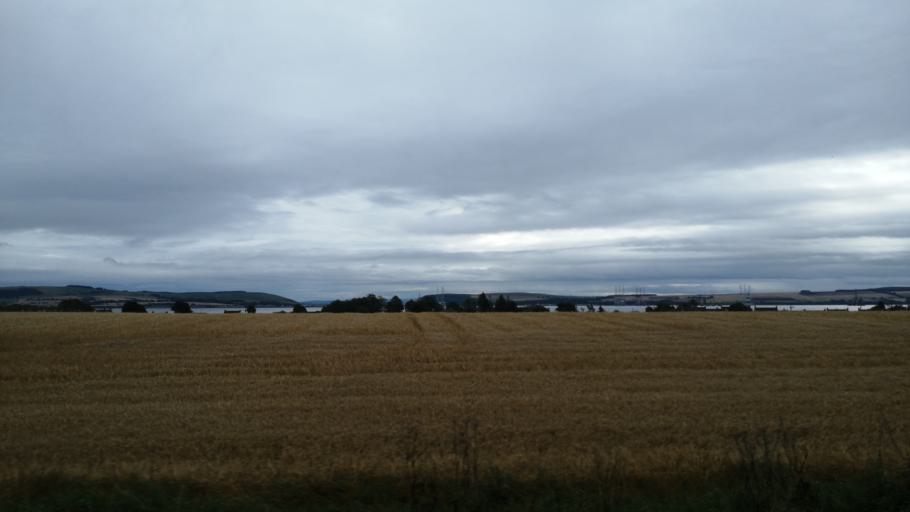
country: GB
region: Scotland
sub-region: Highland
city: Invergordon
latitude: 57.7265
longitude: -4.1062
